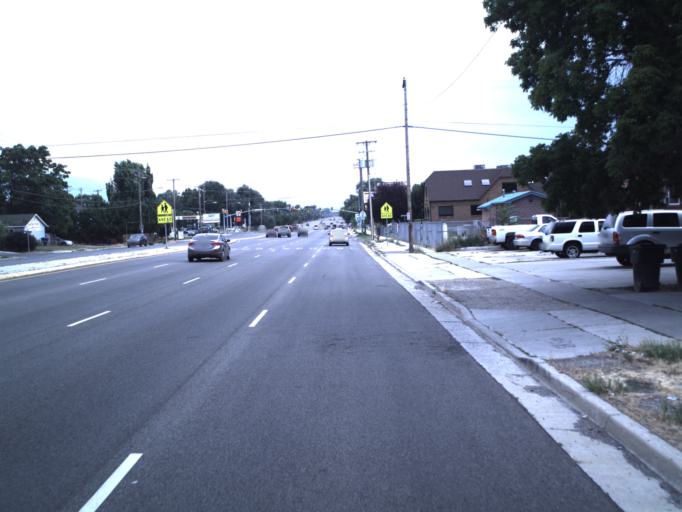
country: US
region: Utah
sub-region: Salt Lake County
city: Millcreek
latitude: 40.7024
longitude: -111.8715
